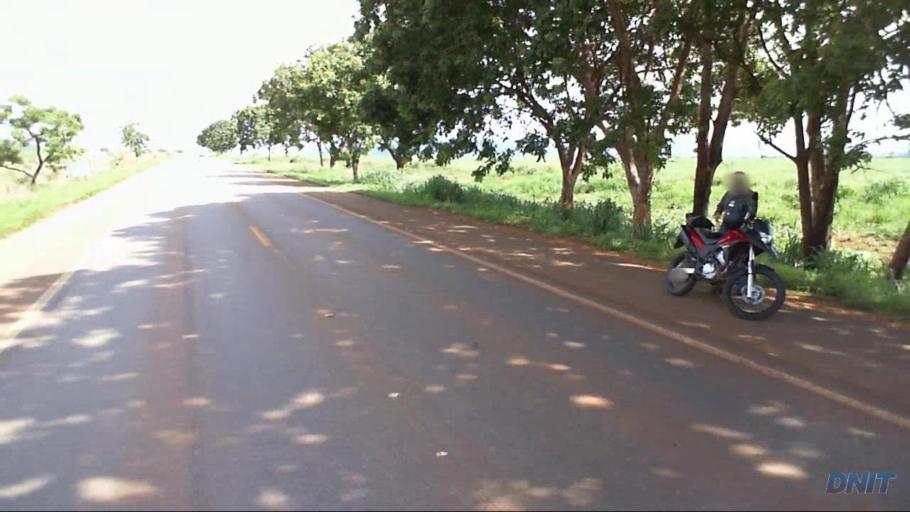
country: BR
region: Goias
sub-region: Barro Alto
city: Barro Alto
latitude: -15.0374
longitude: -48.8912
